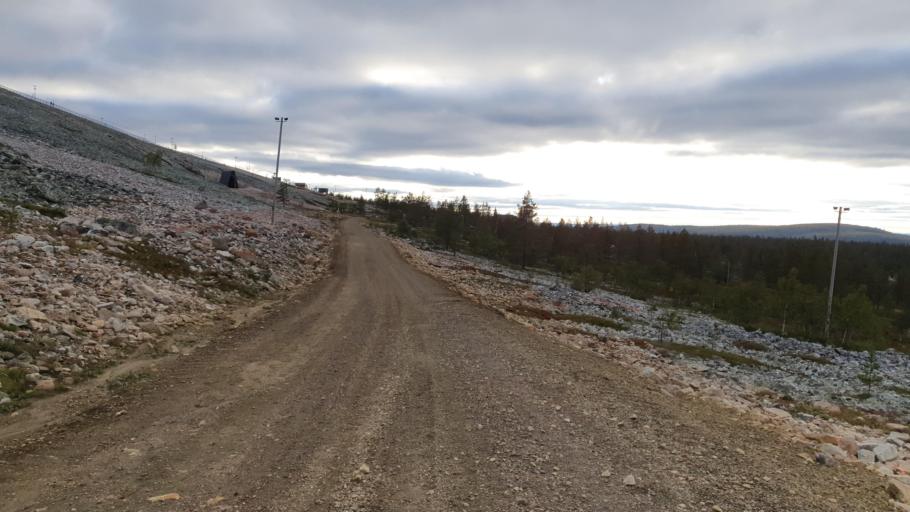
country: FI
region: Lapland
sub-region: Tunturi-Lappi
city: Kolari
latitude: 67.5800
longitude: 24.2169
